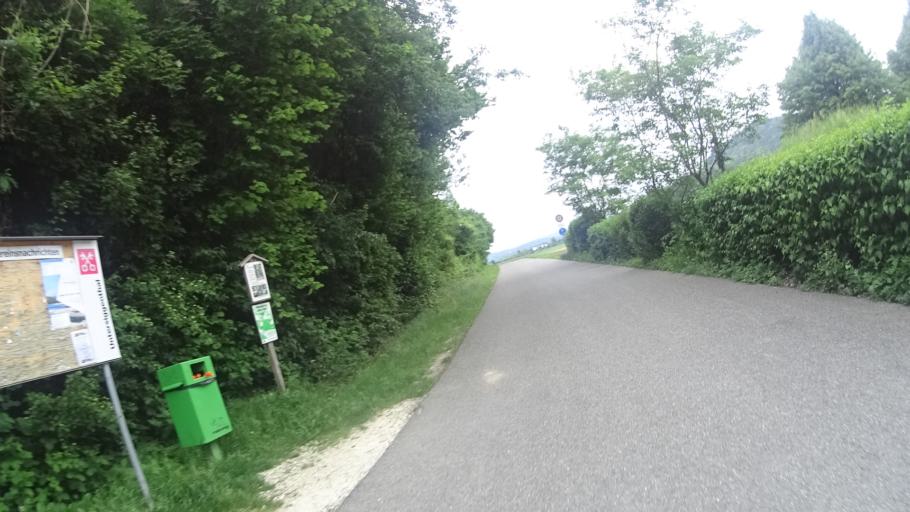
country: CH
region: Aargau
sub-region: Bezirk Brugg
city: Lauffohr (Brugg)
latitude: 47.5158
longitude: 8.2418
